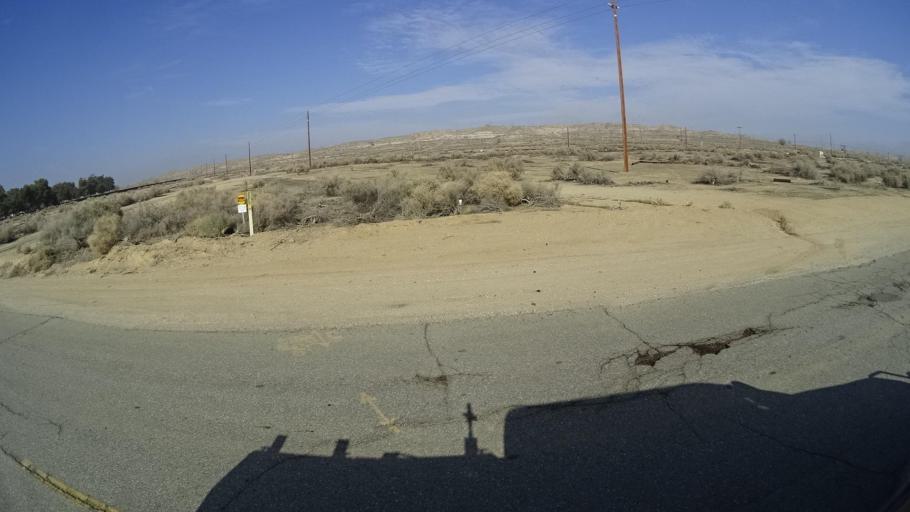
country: US
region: California
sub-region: Kern County
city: Ford City
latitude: 35.1546
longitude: -119.4329
